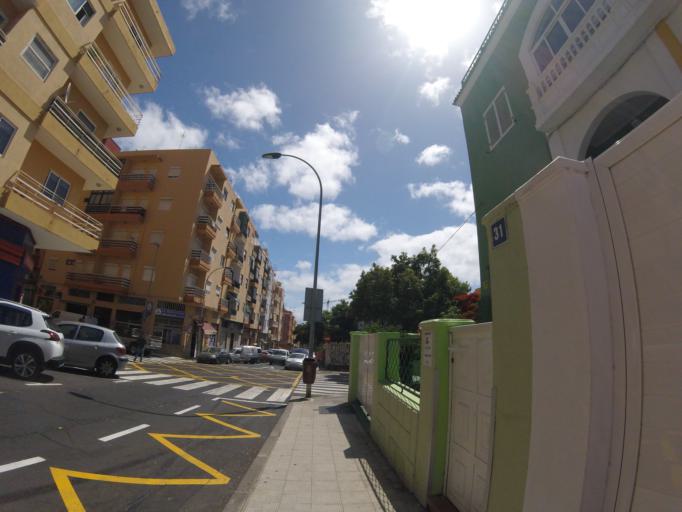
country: ES
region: Canary Islands
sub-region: Provincia de Santa Cruz de Tenerife
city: Santa Cruz de Tenerife
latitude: 28.4627
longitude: -16.2586
